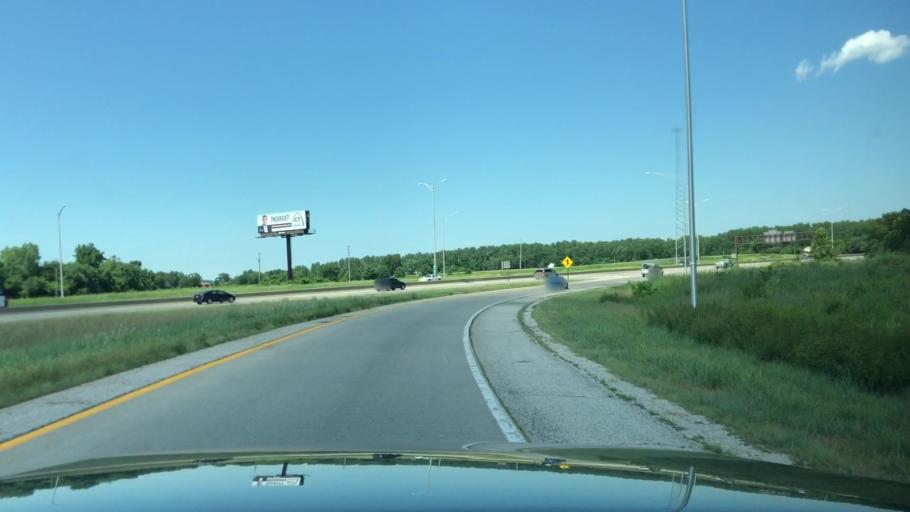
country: US
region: Illinois
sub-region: Saint Clair County
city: Alorton
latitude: 38.5837
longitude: -90.1048
